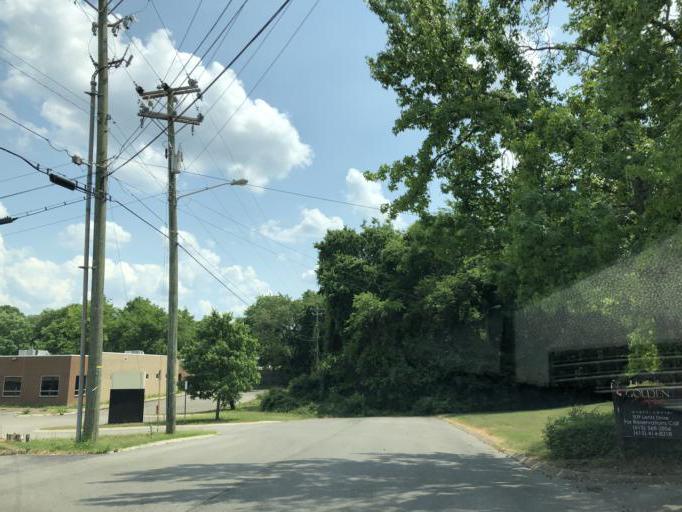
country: US
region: Tennessee
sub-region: Davidson County
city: Goodlettsville
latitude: 36.2484
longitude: -86.7377
